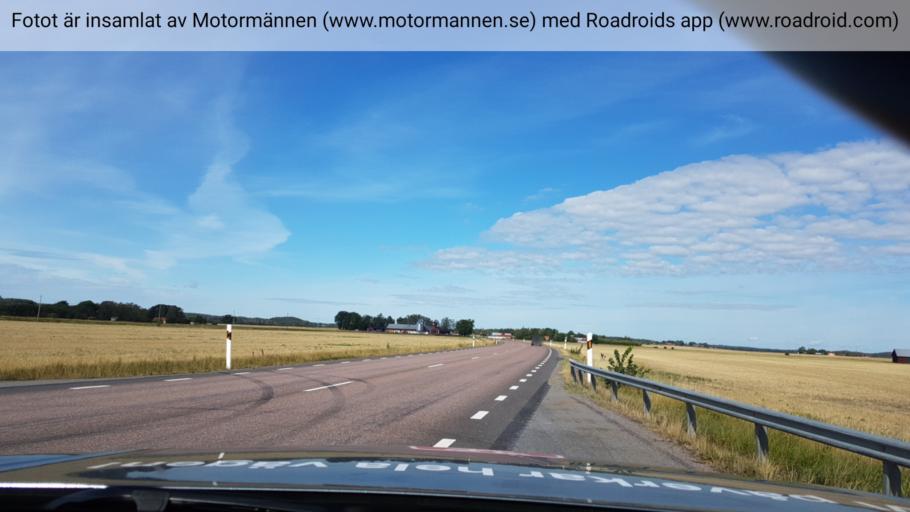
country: SE
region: Uppsala
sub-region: Uppsala Kommun
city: Gamla Uppsala
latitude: 59.9120
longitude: 17.5316
